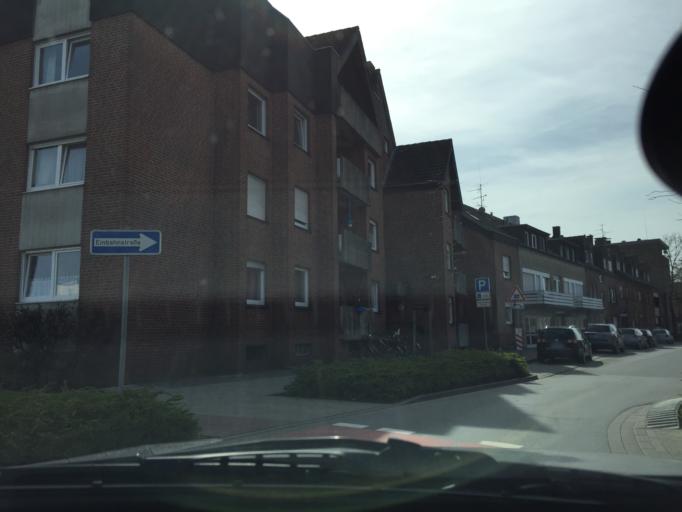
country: DE
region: North Rhine-Westphalia
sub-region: Regierungsbezirk Dusseldorf
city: Goch
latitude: 51.6814
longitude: 6.1596
